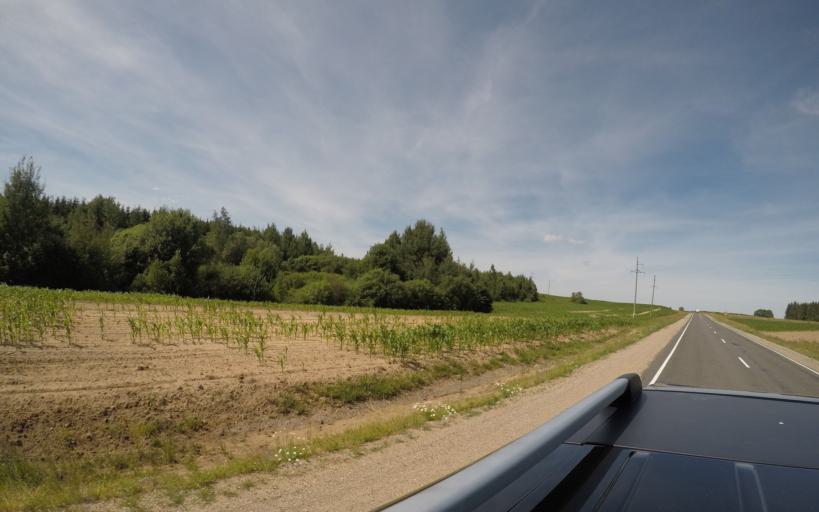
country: BY
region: Grodnenskaya
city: Hal'shany
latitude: 54.2671
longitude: 25.9891
